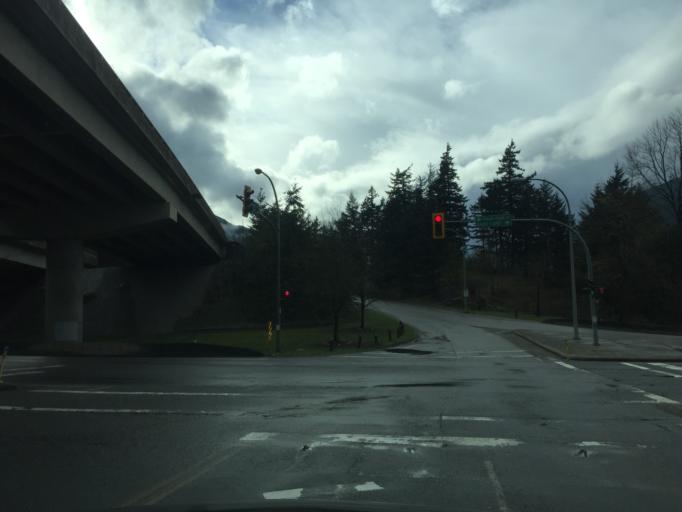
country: CA
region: British Columbia
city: Hope
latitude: 49.3735
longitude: -121.4413
